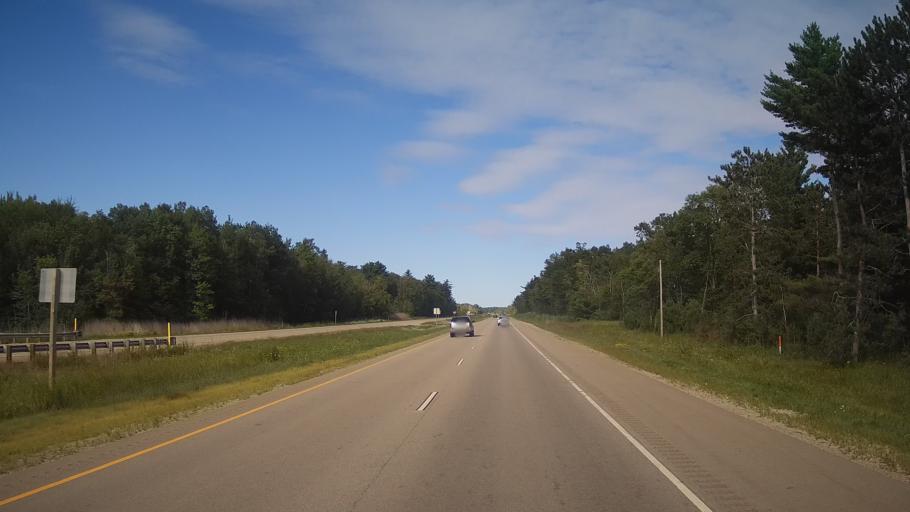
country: US
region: Wisconsin
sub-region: Oconto County
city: Oconto
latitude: 44.8211
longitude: -87.9382
